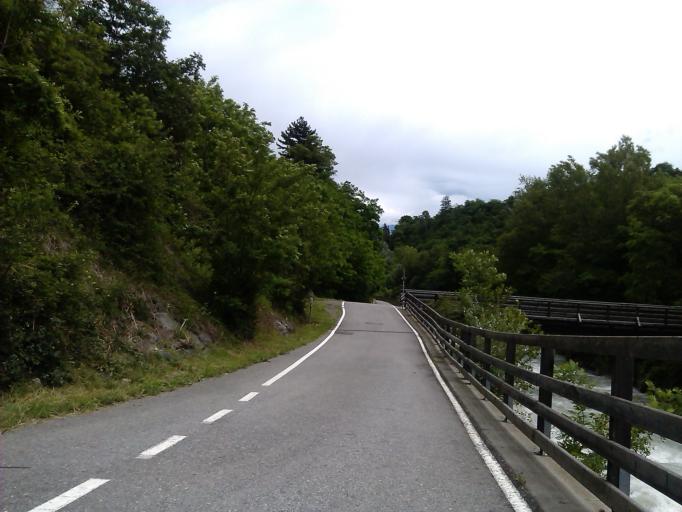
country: IT
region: Trentino-Alto Adige
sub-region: Bolzano
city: Laces
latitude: 46.6241
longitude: 10.8813
